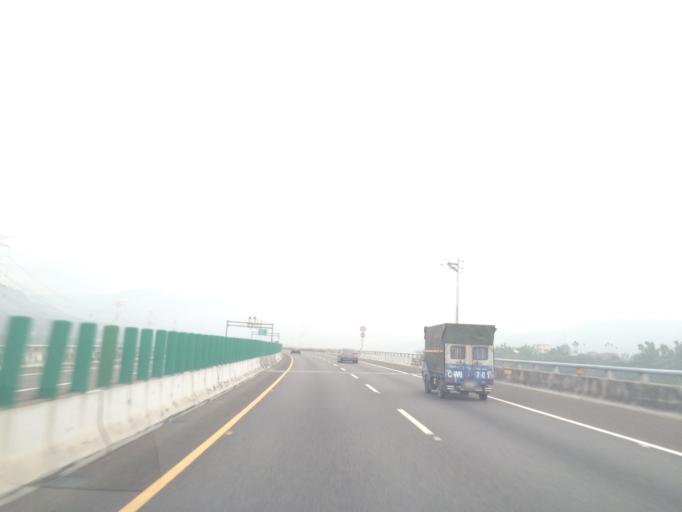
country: TW
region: Taiwan
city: Zhongxing New Village
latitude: 23.9975
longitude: 120.7426
